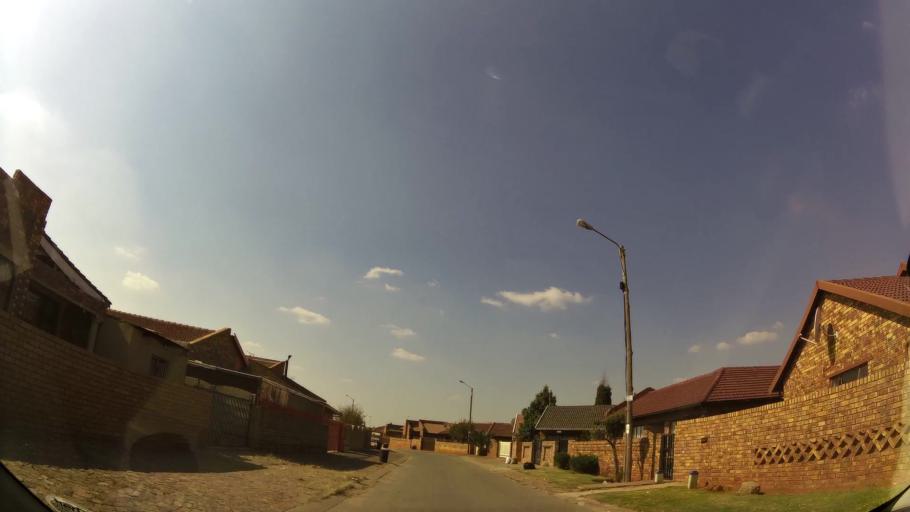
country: ZA
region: Gauteng
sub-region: Ekurhuleni Metropolitan Municipality
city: Benoni
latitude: -26.1472
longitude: 28.4005
